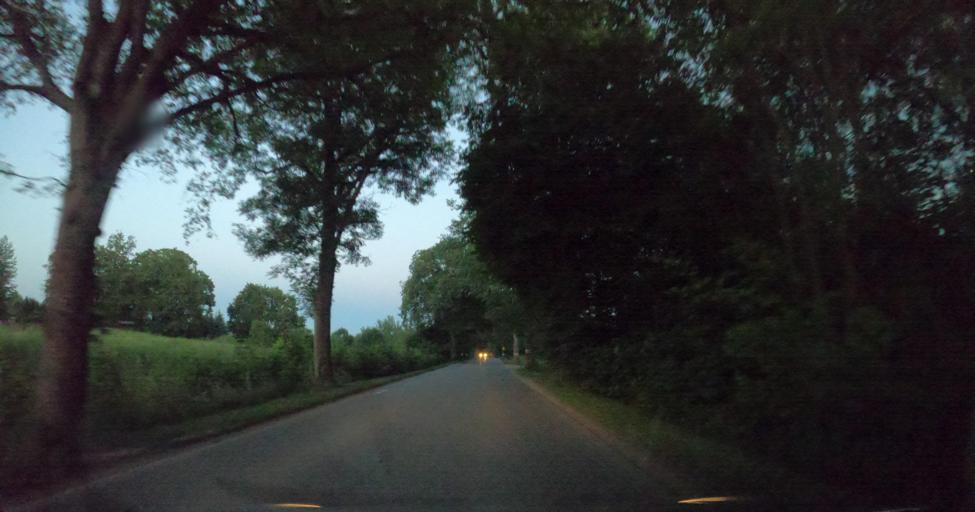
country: PL
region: Pomeranian Voivodeship
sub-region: Powiat wejherowski
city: Szemud
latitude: 54.4739
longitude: 18.2720
